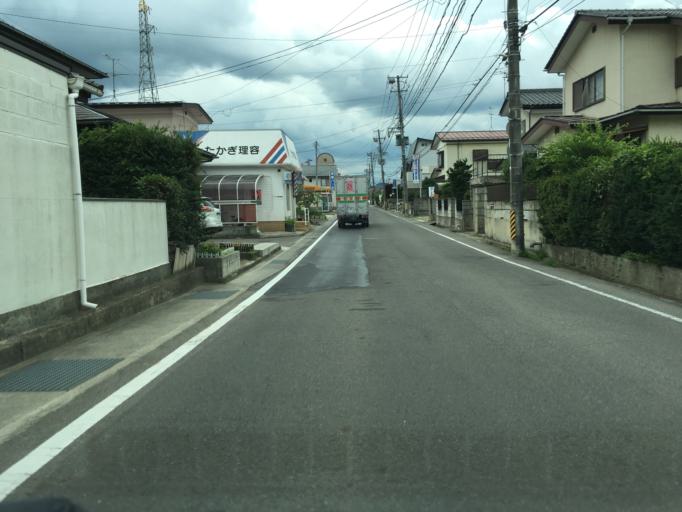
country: JP
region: Fukushima
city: Fukushima-shi
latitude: 37.7321
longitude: 140.4481
